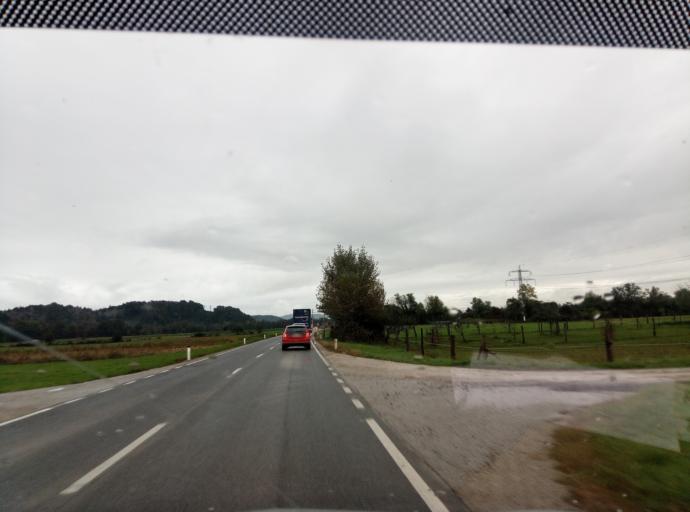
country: SI
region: Ljubljana
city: Ljubljana
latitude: 46.1033
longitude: 14.4990
